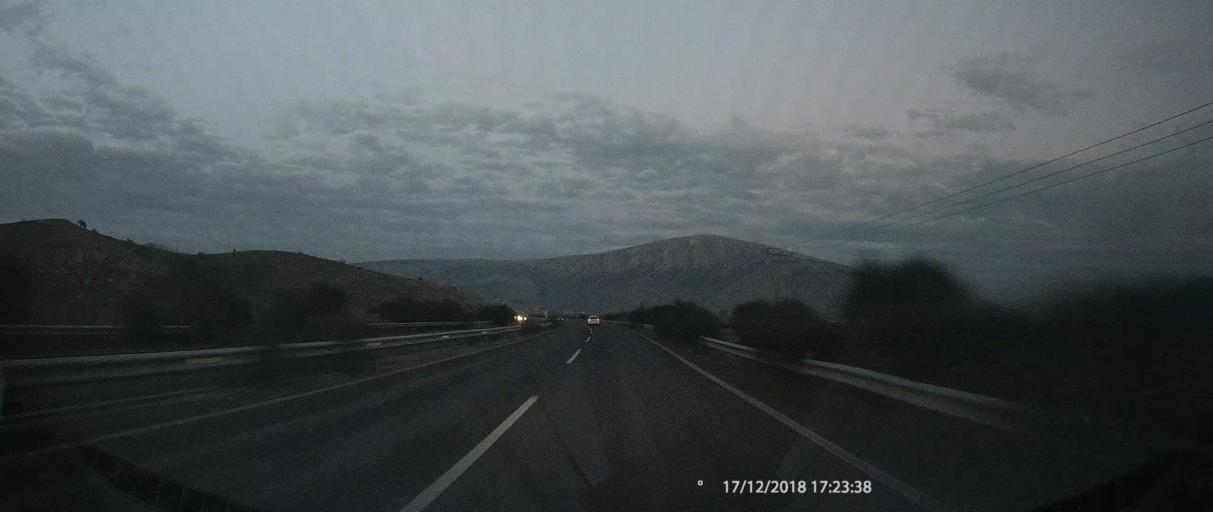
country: GR
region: Thessaly
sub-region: Trikala
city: Farkadona
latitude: 39.5925
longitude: 22.0921
